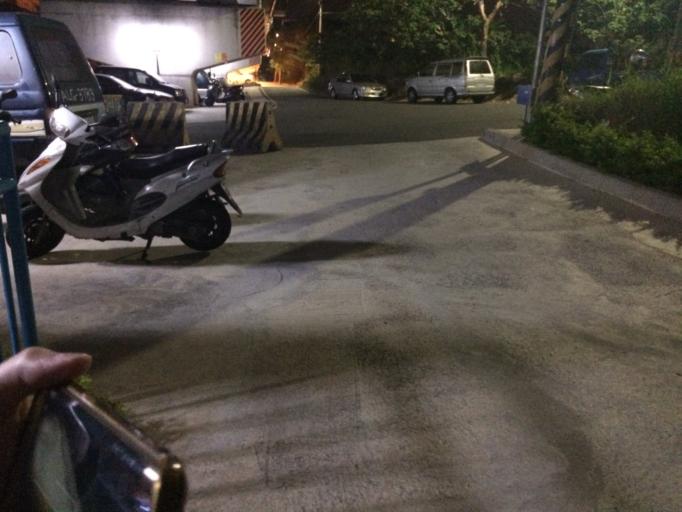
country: TW
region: Taiwan
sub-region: Hsinchu
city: Zhubei
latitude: 24.7857
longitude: 121.0226
